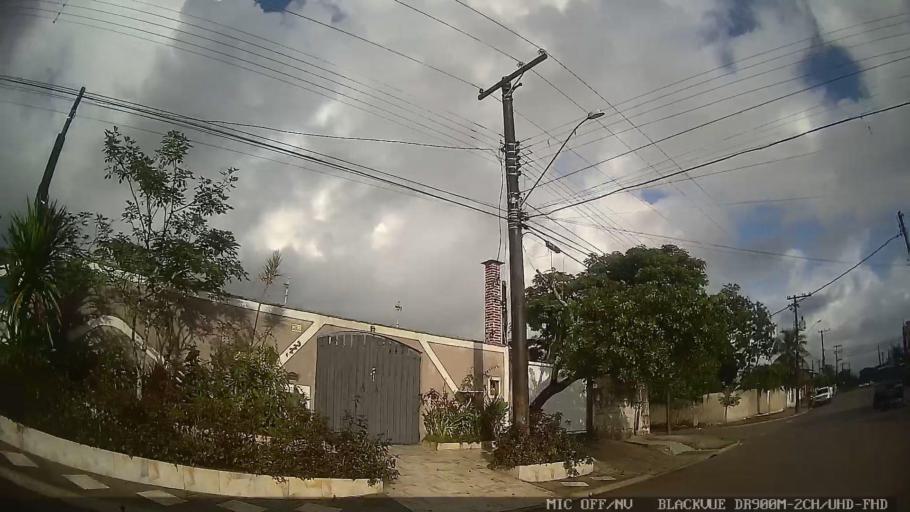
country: BR
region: Sao Paulo
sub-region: Itanhaem
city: Itanhaem
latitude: -24.1863
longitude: -46.8592
